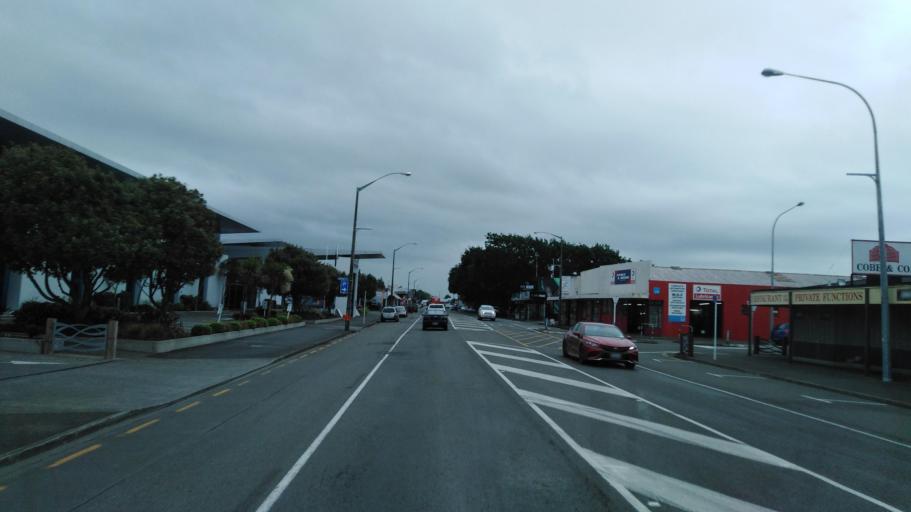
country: NZ
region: Manawatu-Wanganui
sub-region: Horowhenua District
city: Levin
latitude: -40.6244
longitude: 175.2841
